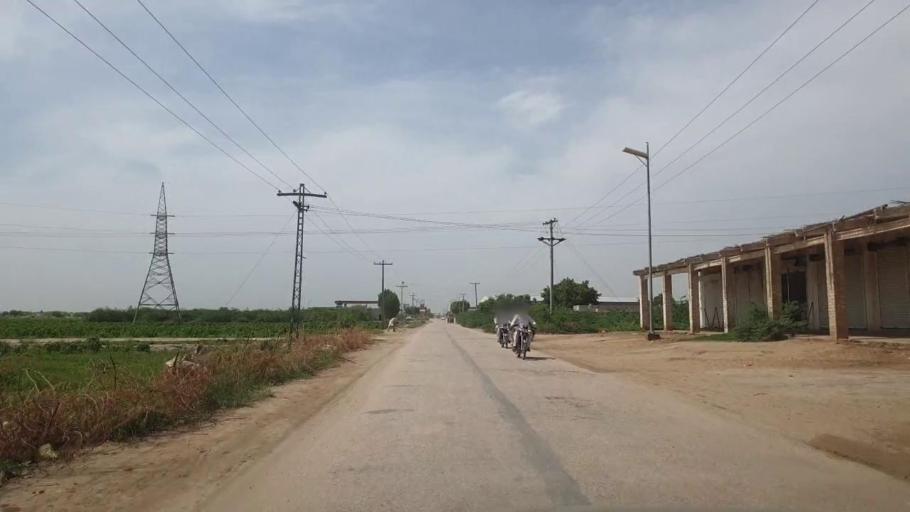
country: PK
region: Sindh
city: Kot Diji
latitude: 27.1505
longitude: 68.9632
